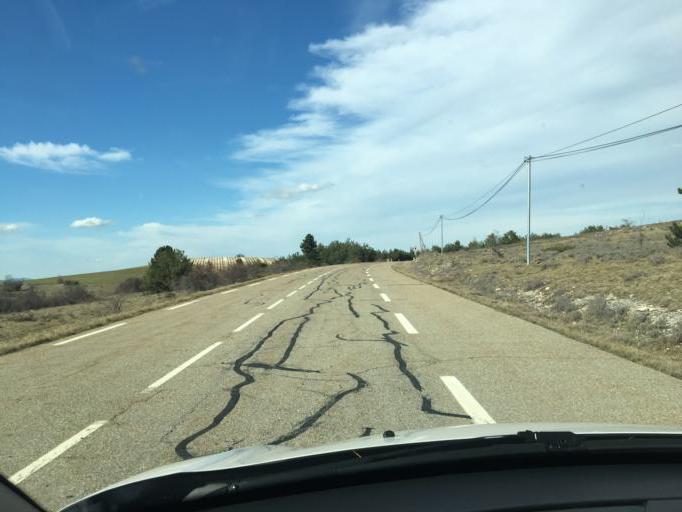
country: FR
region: Provence-Alpes-Cote d'Azur
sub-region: Departement du Vaucluse
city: Saint-Saturnin-les-Apt
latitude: 43.9931
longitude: 5.4773
